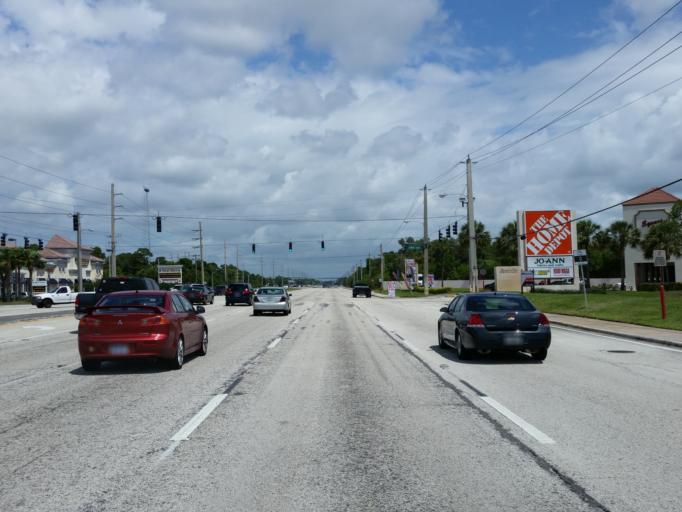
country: US
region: Florida
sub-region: Martin County
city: North River Shores
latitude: 27.2478
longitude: -80.2734
